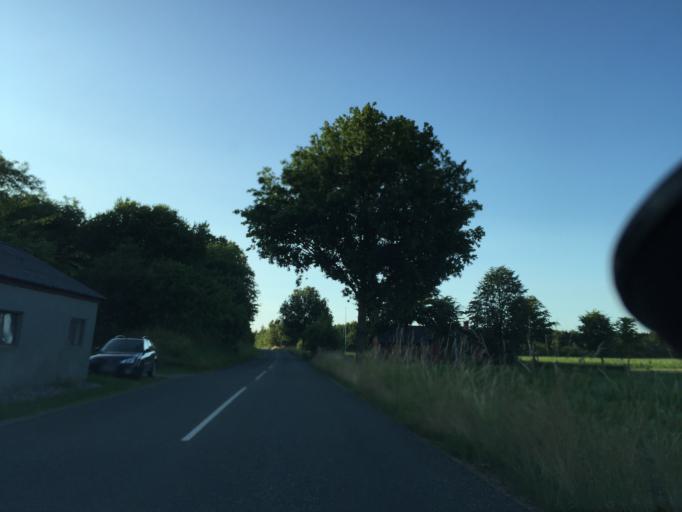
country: DK
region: Central Jutland
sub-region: Silkeborg Kommune
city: Svejbaek
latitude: 56.2289
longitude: 9.6656
